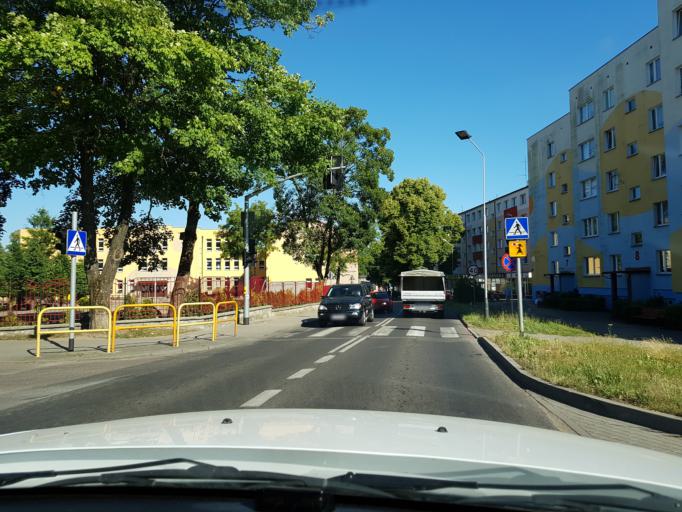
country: PL
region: West Pomeranian Voivodeship
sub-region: Powiat lobeski
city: Lobez
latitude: 53.6416
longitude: 15.6204
